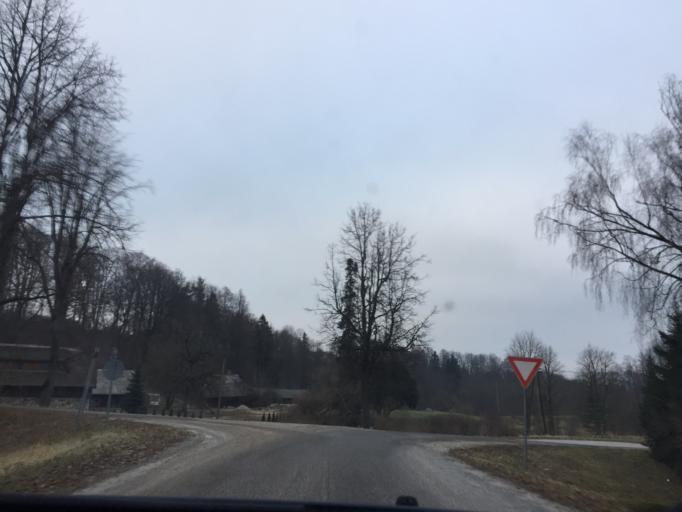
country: LV
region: Raunas
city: Rauna
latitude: 57.3269
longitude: 25.6014
